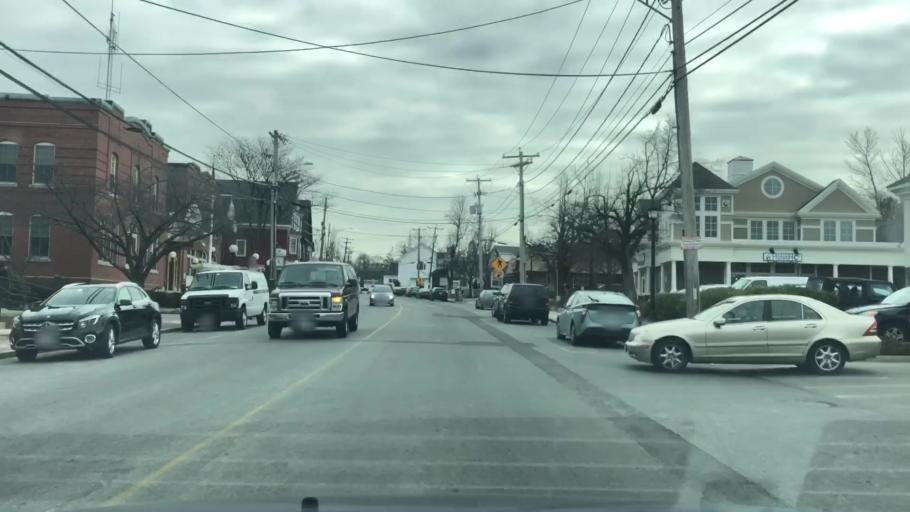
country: US
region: Massachusetts
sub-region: Essex County
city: North Andover
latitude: 42.7033
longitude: -71.1316
